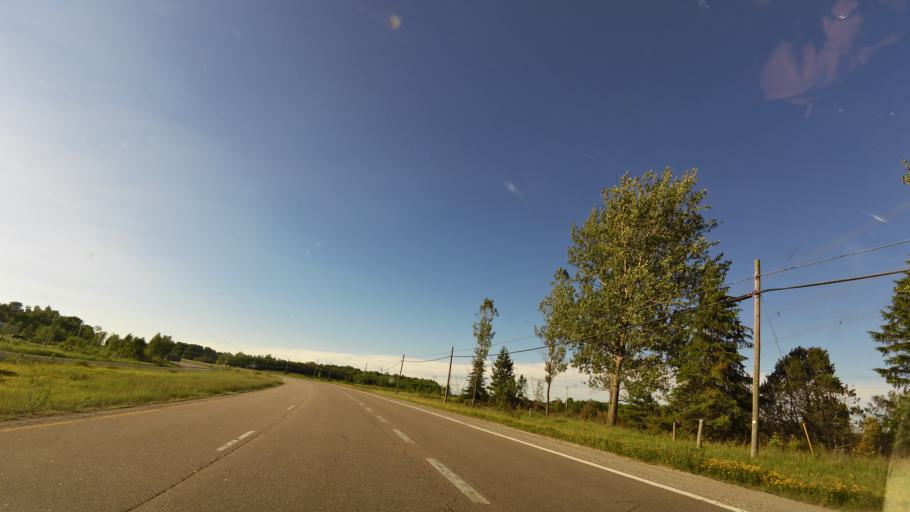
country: CA
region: Ontario
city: Midland
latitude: 44.7725
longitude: -79.6907
